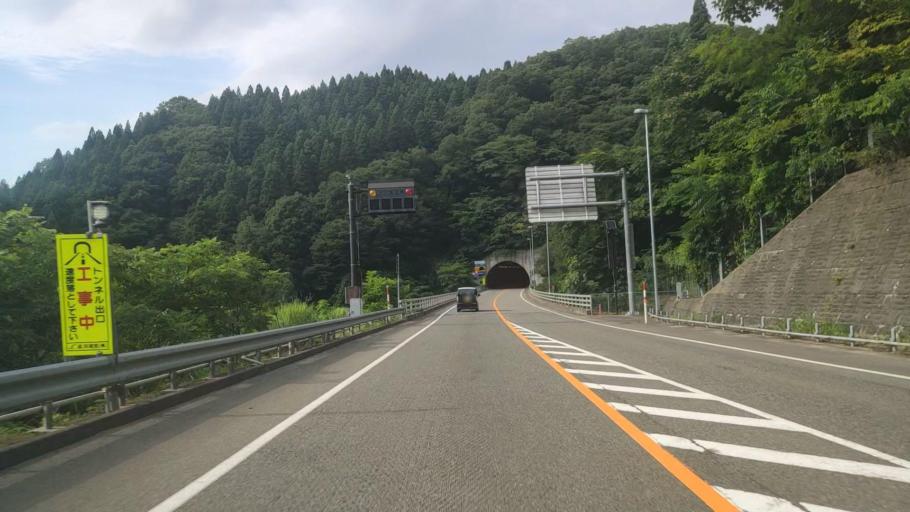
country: JP
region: Fukui
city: Takefu
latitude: 35.8186
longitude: 136.1018
